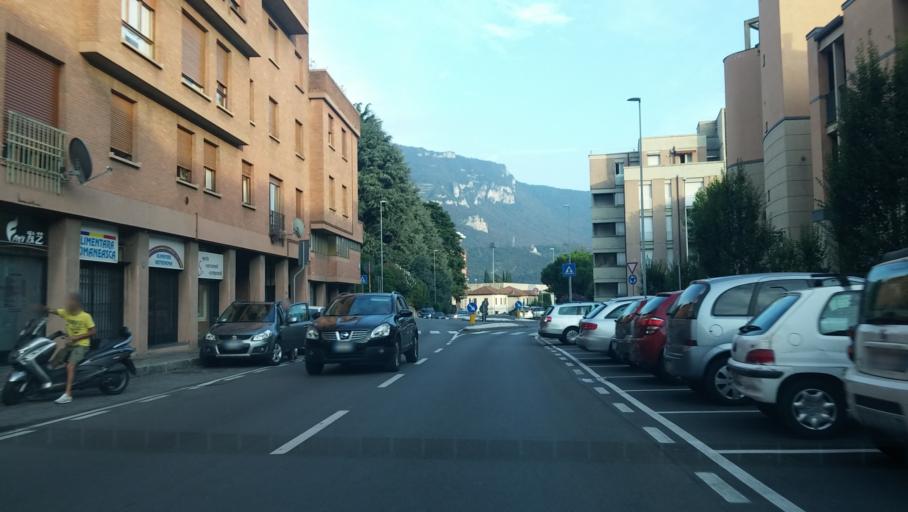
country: IT
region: Lombardy
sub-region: Provincia di Lecco
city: Lecco
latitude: 45.8594
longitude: 9.3956
